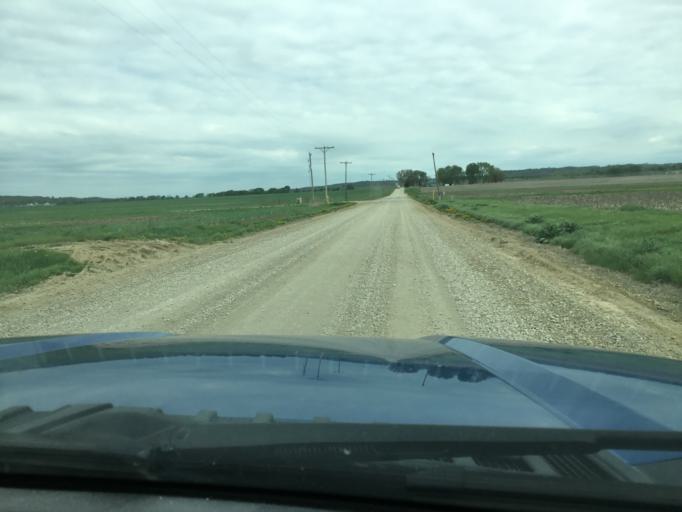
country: US
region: Kansas
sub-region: Douglas County
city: Lawrence
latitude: 39.0141
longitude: -95.2242
